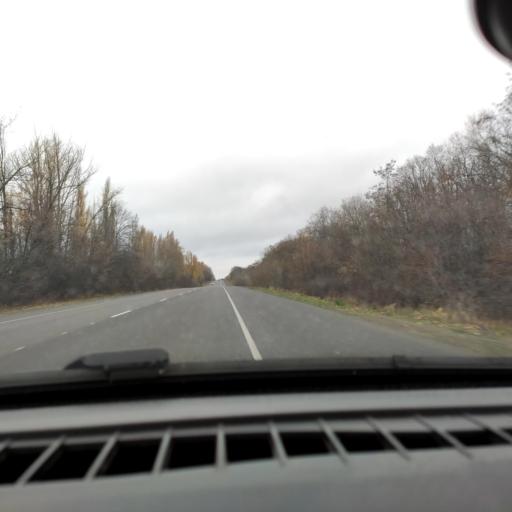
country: RU
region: Voronezj
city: Kolodeznyy
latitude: 51.2485
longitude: 39.0551
